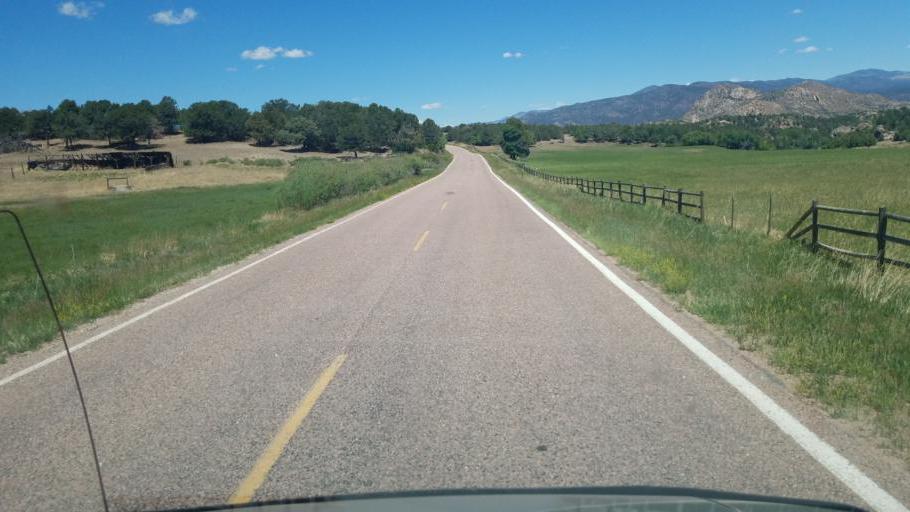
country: US
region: Colorado
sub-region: Custer County
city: Westcliffe
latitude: 38.3165
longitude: -105.6615
